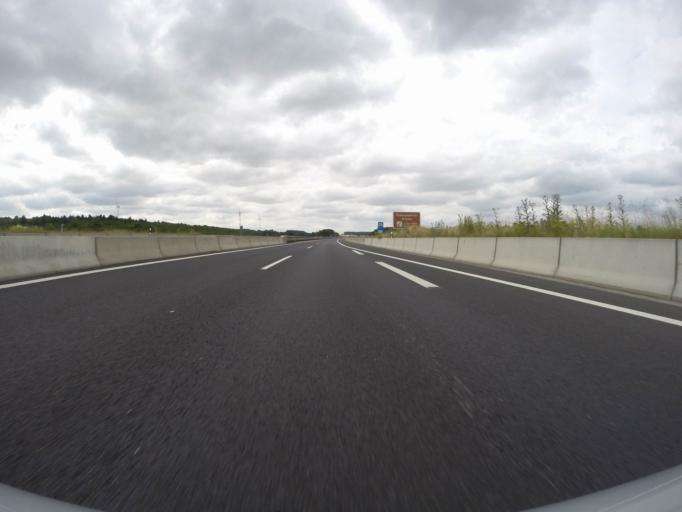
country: DE
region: Bavaria
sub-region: Regierungsbezirk Unterfranken
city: Rannungen
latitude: 50.1974
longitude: 10.2143
